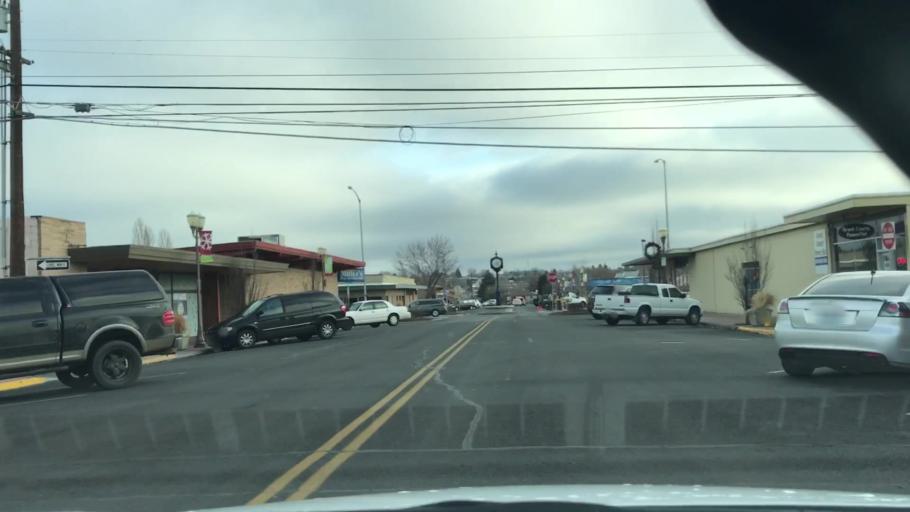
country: US
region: Washington
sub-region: Grant County
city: Moses Lake
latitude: 47.1301
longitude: -119.2800
